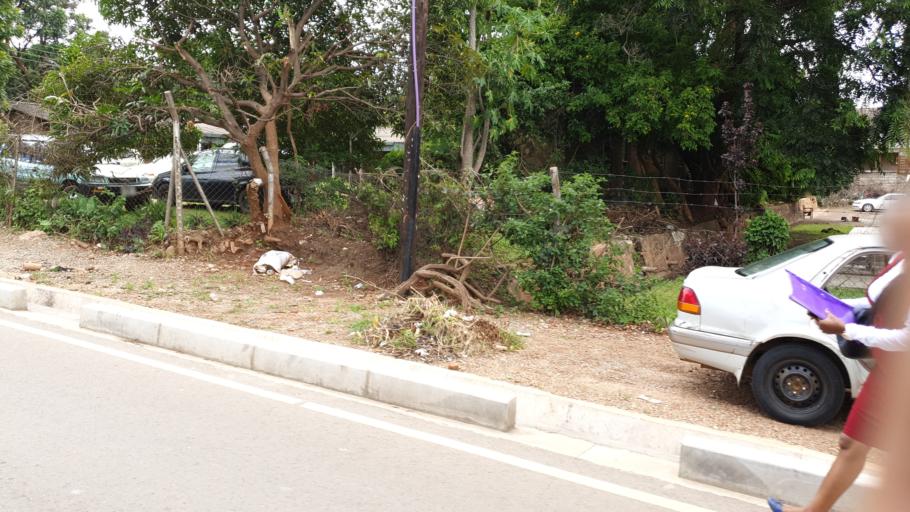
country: ZM
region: Lusaka
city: Lusaka
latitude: -15.4260
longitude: 28.3092
